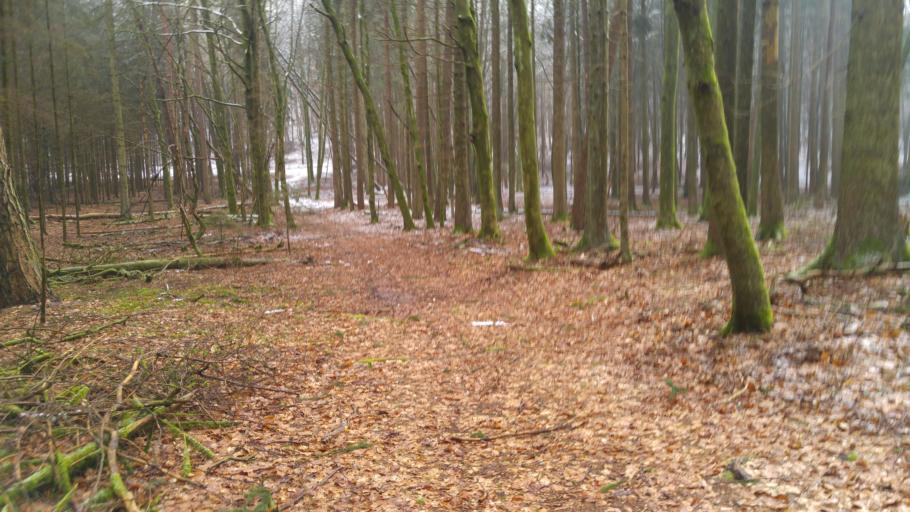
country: DE
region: Rheinland-Pfalz
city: Vorderweidenthal
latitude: 49.1117
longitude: 7.8996
